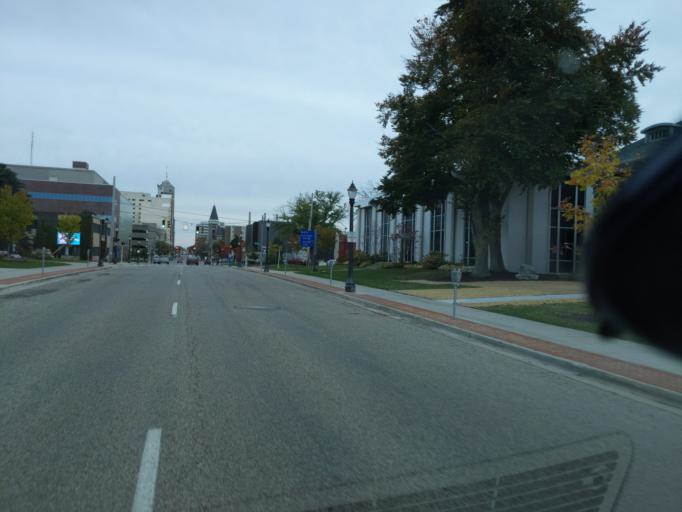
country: US
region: Michigan
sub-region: Ingham County
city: Lansing
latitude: 42.7393
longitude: -84.5538
